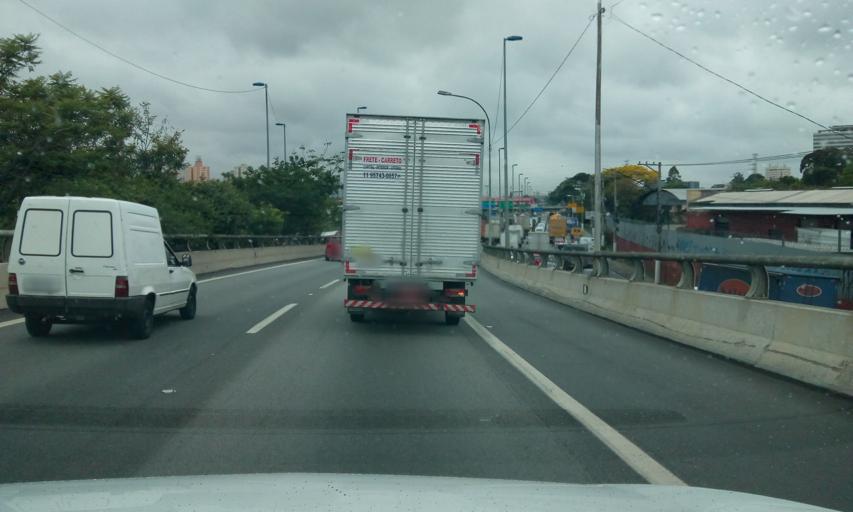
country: BR
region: Sao Paulo
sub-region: Osasco
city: Osasco
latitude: -23.5089
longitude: -46.7177
